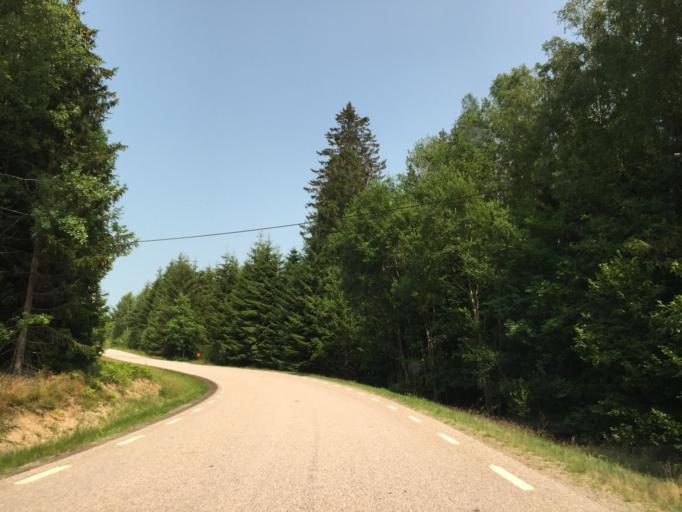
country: SE
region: Vaestra Goetaland
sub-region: Lilla Edets Kommun
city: Lilla Edet
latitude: 58.1587
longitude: 12.0687
